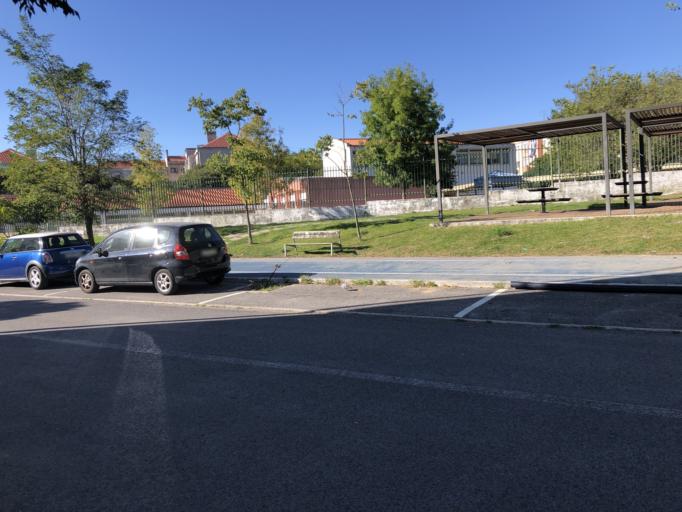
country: PT
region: Lisbon
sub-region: Sintra
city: Queluz
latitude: 38.7570
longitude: -9.2449
